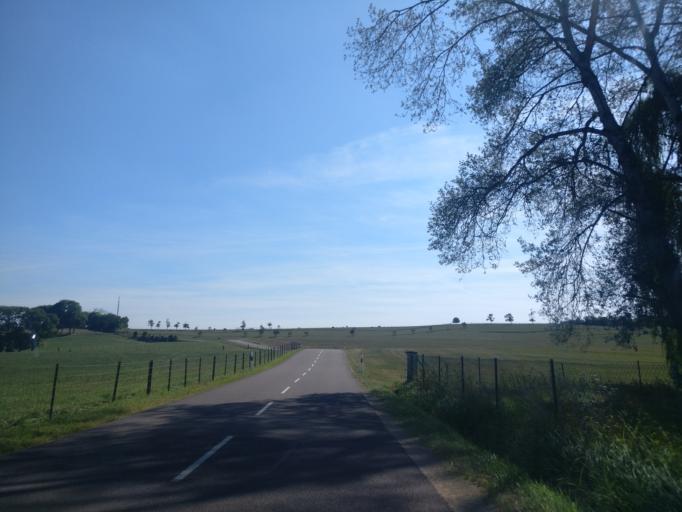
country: LU
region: Grevenmacher
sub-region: Canton de Grevenmacher
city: Flaxweiler
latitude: 49.6703
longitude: 6.3310
